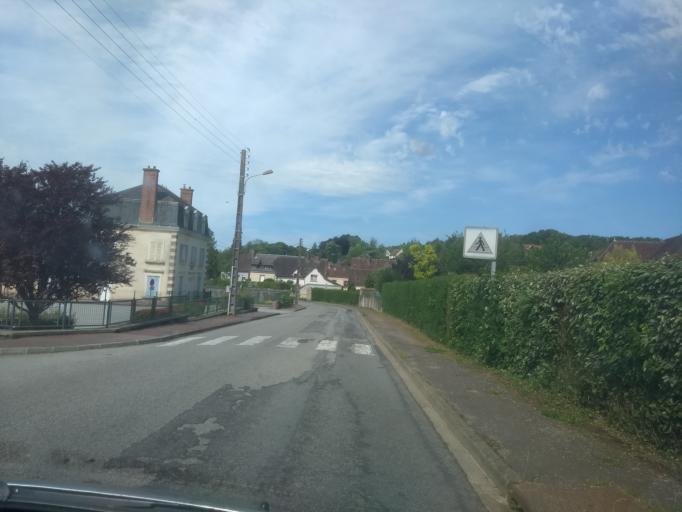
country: FR
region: Lower Normandy
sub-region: Departement de l'Orne
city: Longny-au-Perche
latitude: 48.5274
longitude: 0.7545
